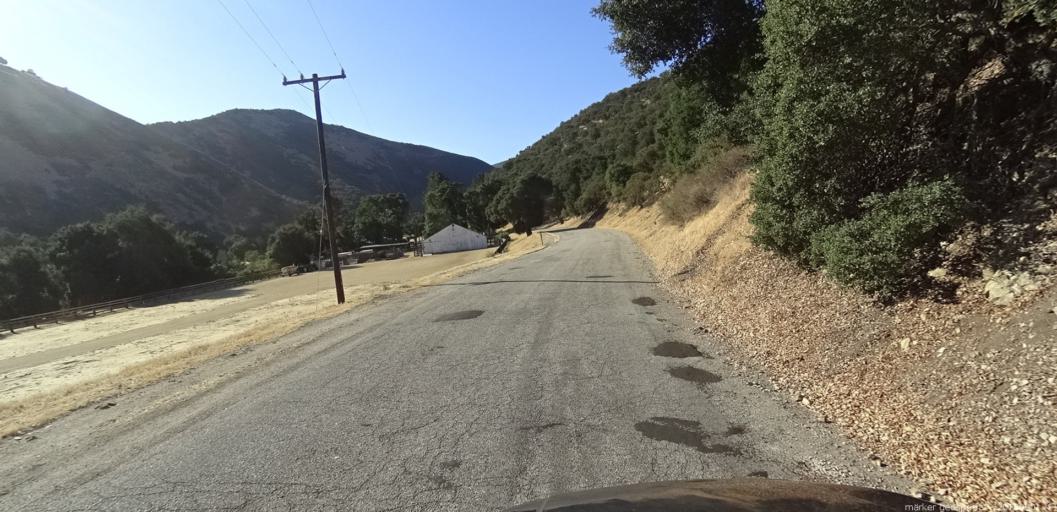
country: US
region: California
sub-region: Monterey County
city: Greenfield
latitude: 36.2063
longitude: -121.2781
